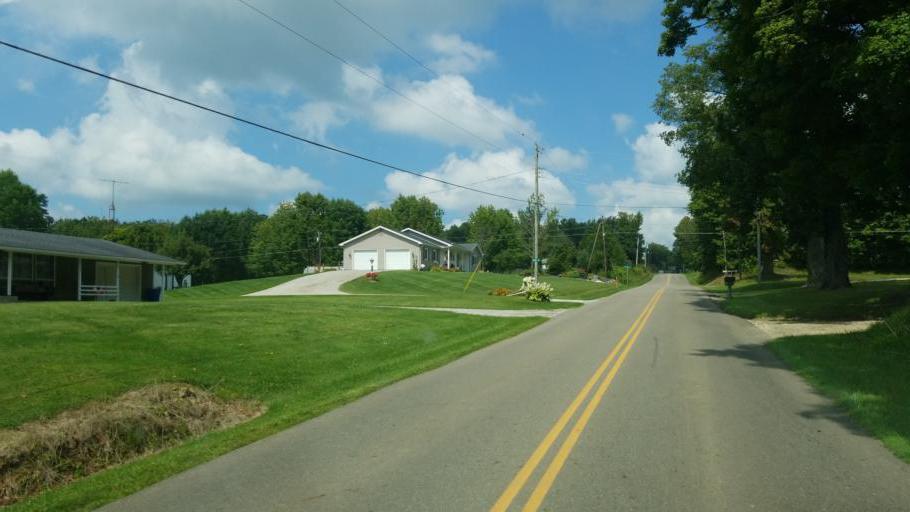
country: US
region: Ohio
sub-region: Knox County
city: Mount Vernon
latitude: 40.4260
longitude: -82.4879
